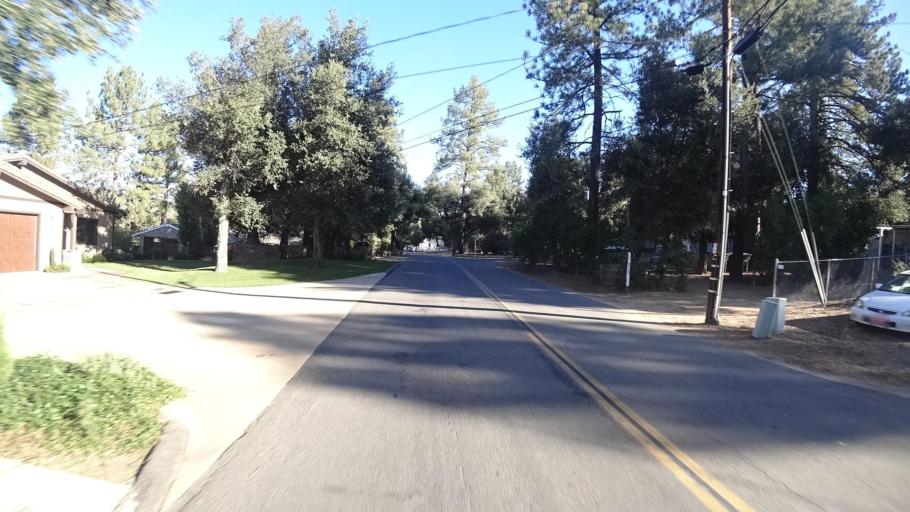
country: US
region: California
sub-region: San Diego County
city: Pine Valley
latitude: 32.8347
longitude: -116.5275
